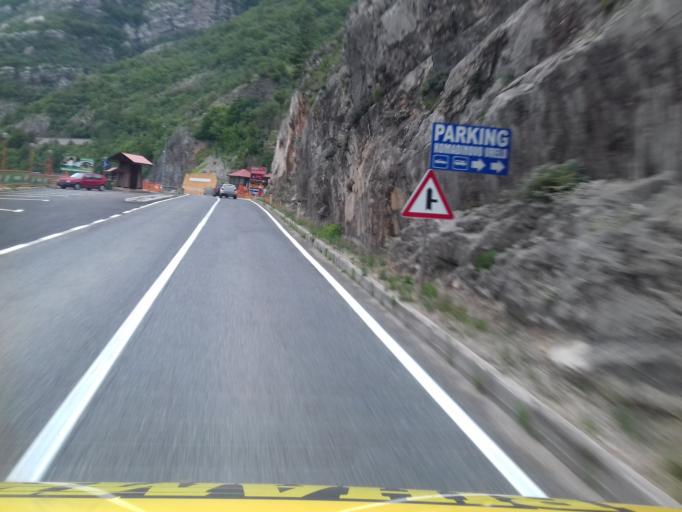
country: BA
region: Federation of Bosnia and Herzegovina
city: Jablanica
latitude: 43.6171
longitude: 17.7407
